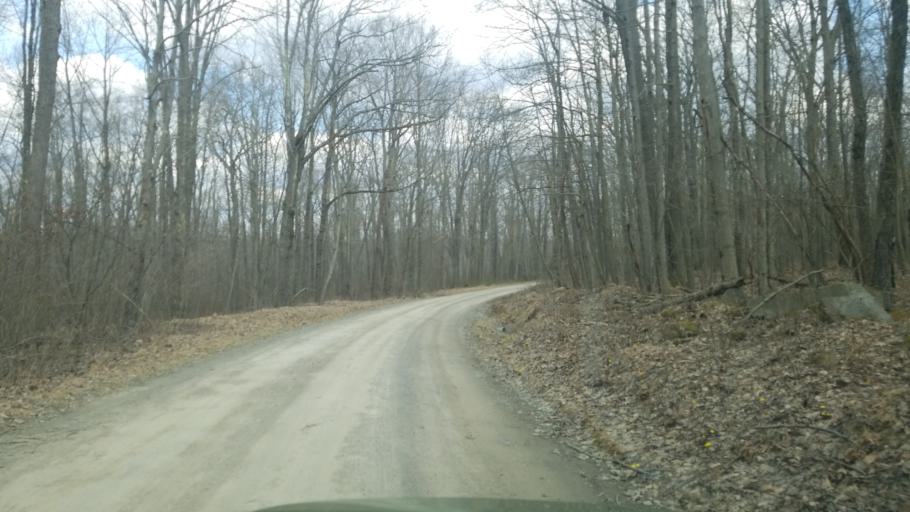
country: US
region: Pennsylvania
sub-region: Clearfield County
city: Clearfield
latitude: 41.1712
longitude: -78.4928
